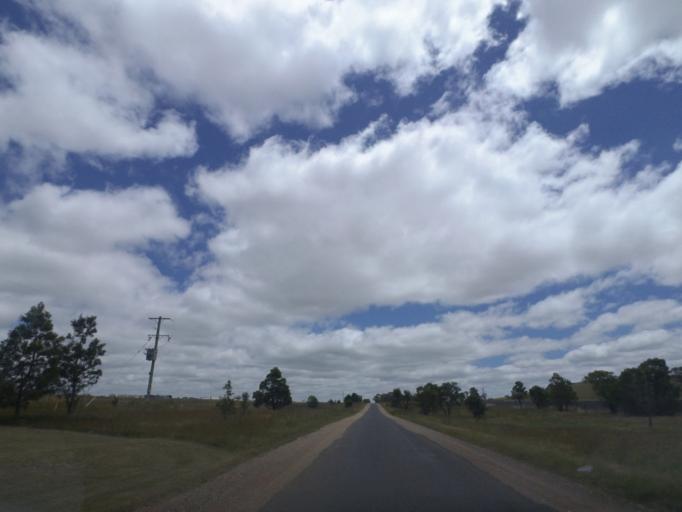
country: AU
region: Victoria
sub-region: Moorabool
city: Bacchus Marsh
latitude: -37.6181
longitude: 144.2527
